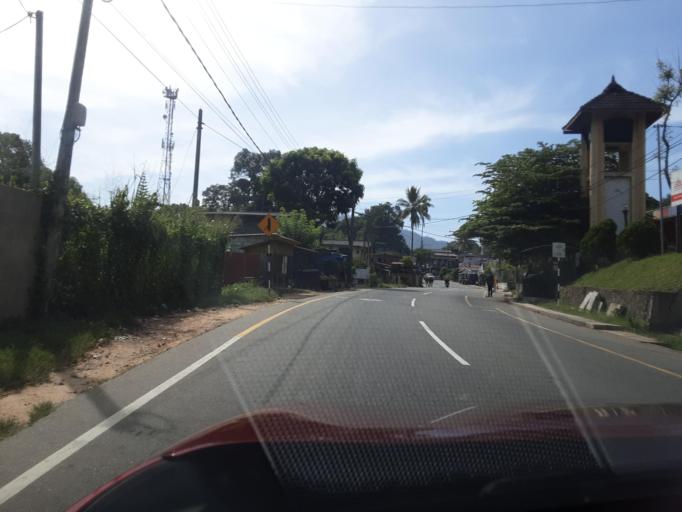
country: LK
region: Uva
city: Badulla
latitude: 6.9789
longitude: 81.0826
